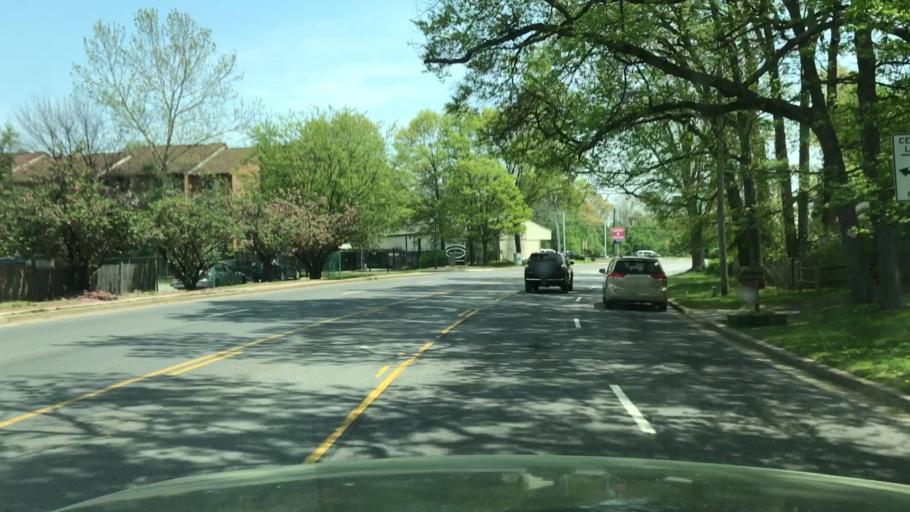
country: US
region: Maryland
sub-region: Anne Arundel County
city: Robinwood
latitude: 38.9676
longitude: -76.5146
